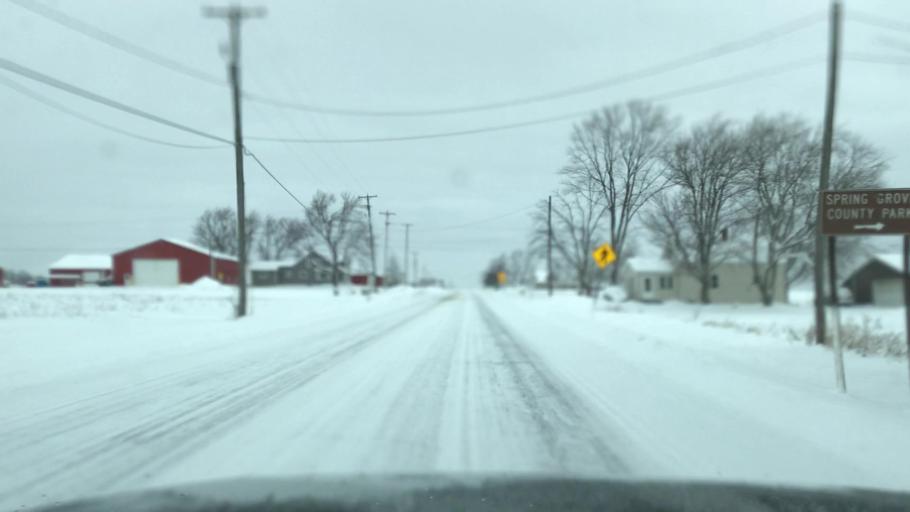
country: US
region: Michigan
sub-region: Ottawa County
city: Hudsonville
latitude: 42.8319
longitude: -85.8421
